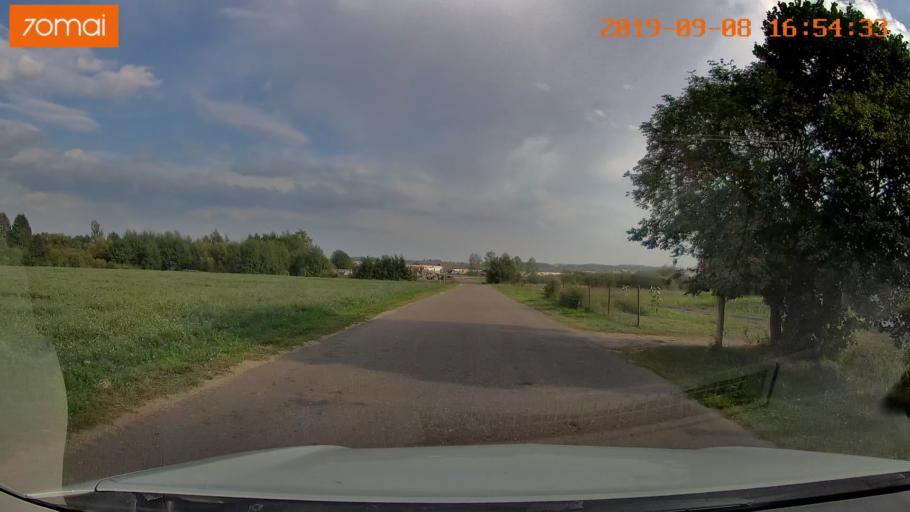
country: BY
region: Grodnenskaya
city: Hrodna
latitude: 53.7508
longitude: 23.9198
